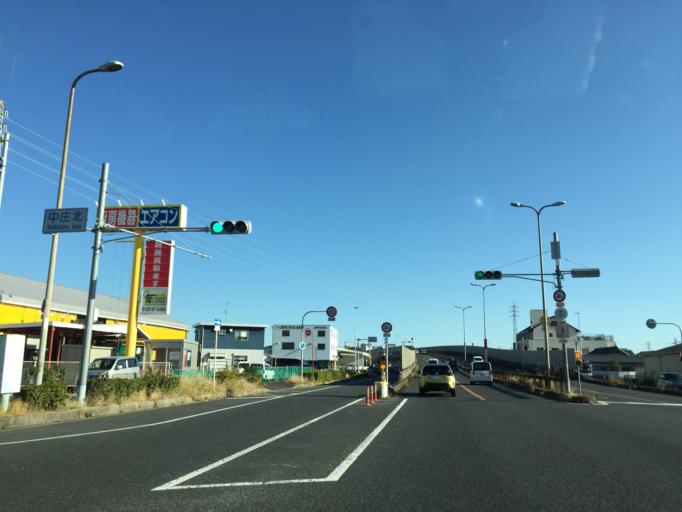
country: JP
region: Osaka
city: Kaizuka
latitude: 34.4126
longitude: 135.3320
